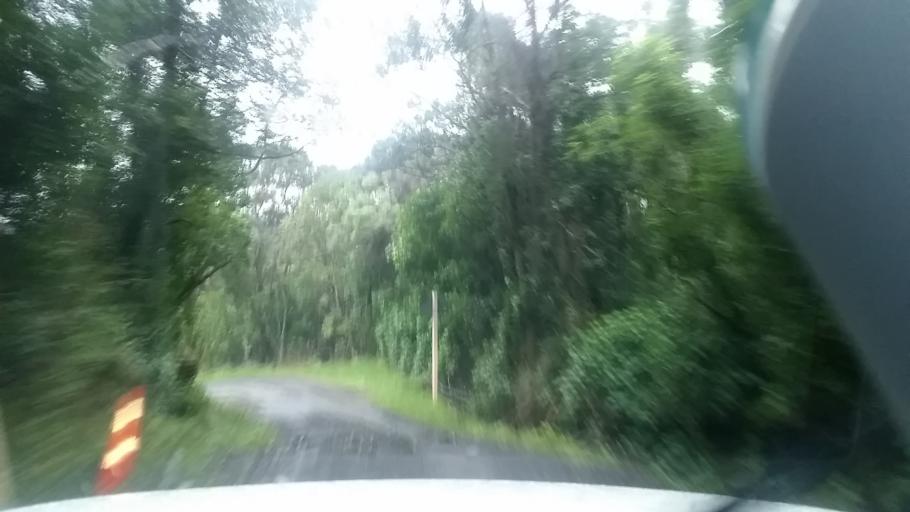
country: NZ
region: Canterbury
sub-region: Christchurch City
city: Christchurch
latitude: -43.8081
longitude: 172.8919
